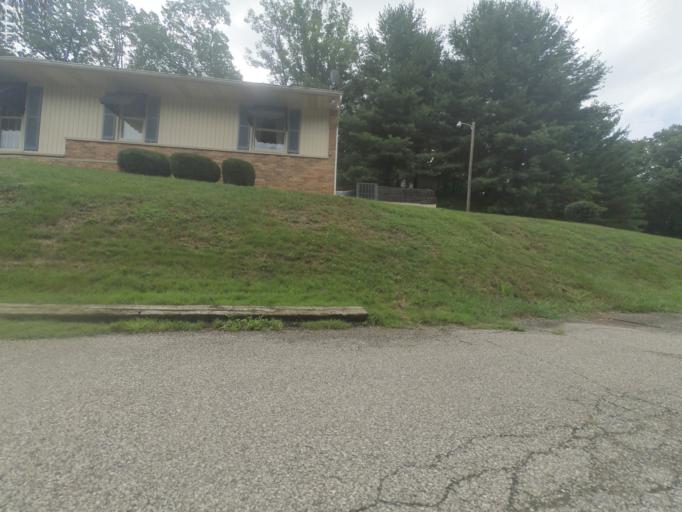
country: US
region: West Virginia
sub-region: Cabell County
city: Huntington
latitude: 38.3975
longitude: -82.4013
